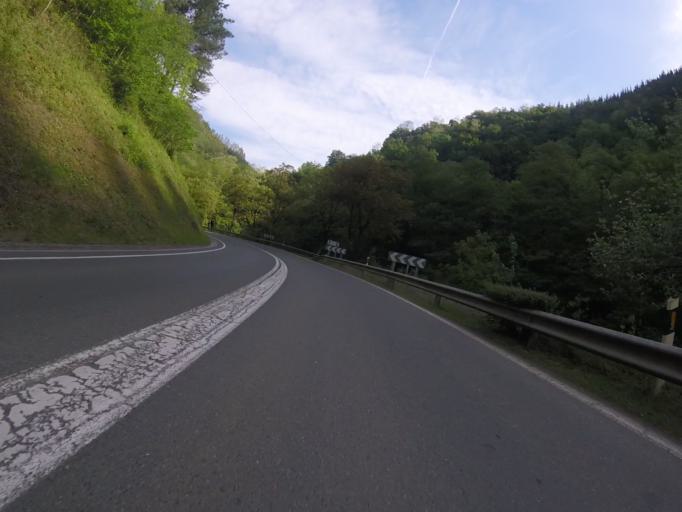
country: ES
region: Basque Country
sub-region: Provincia de Guipuzcoa
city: Azkoitia
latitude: 43.1406
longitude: -2.3482
